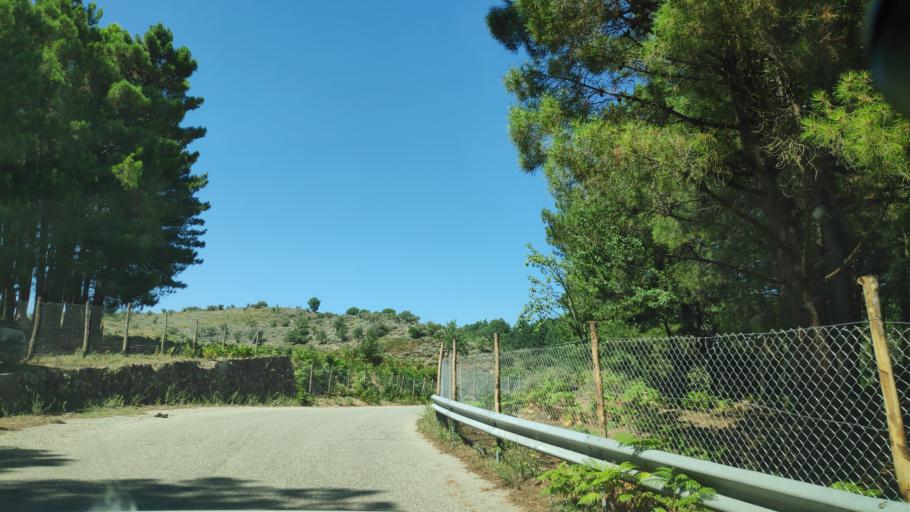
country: IT
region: Calabria
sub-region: Provincia di Reggio Calabria
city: Bova
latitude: 38.0157
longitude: 15.9346
